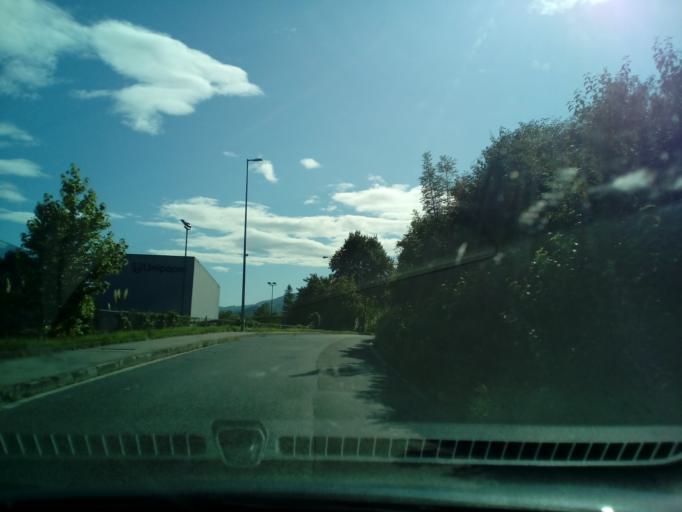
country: ES
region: Basque Country
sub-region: Provincia de Guipuzcoa
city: Aduna
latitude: 43.2023
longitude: -2.0449
